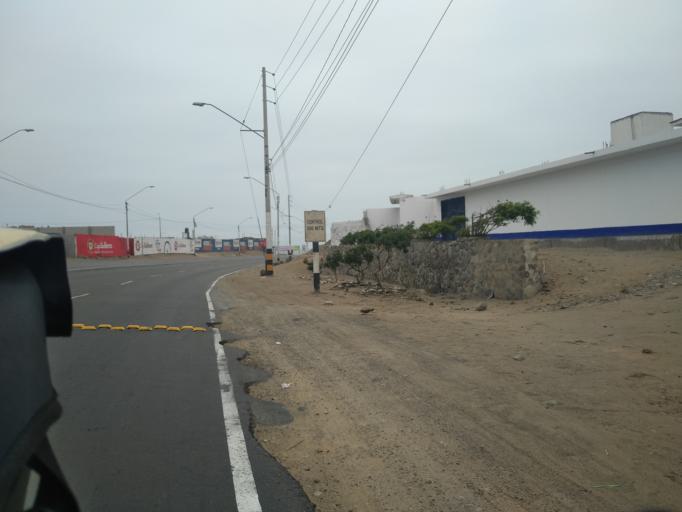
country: PE
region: La Libertad
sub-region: Provincia de Trujillo
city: Huanchaco
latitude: -8.0968
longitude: -79.1092
